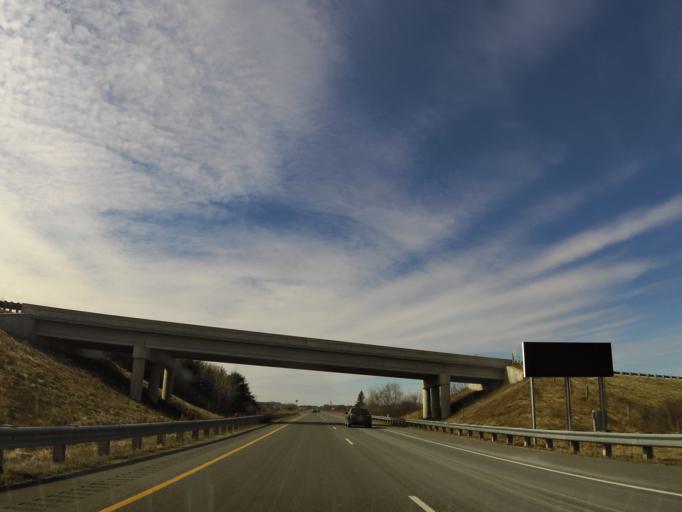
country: US
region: Wisconsin
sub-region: Monroe County
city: Tomah
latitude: 43.9542
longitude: -90.3467
